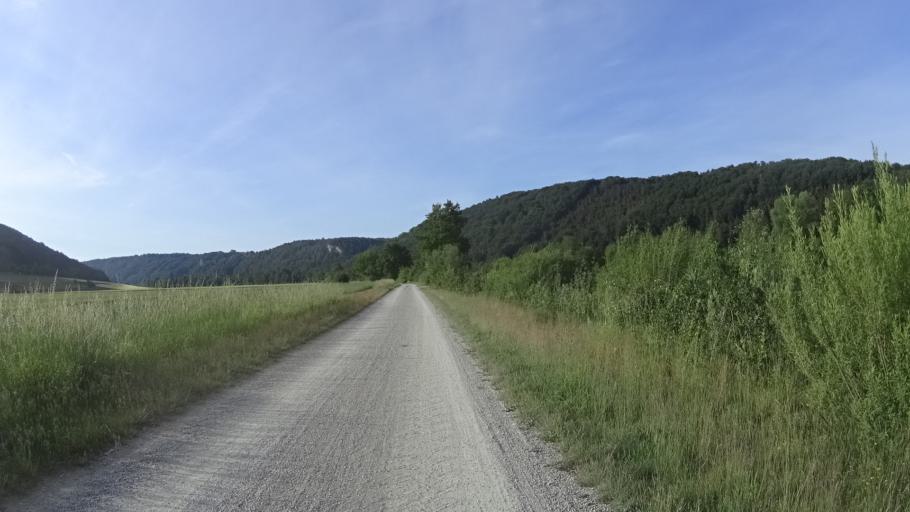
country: DE
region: Bavaria
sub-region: Lower Bavaria
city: Riedenburg
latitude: 48.9861
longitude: 11.6330
